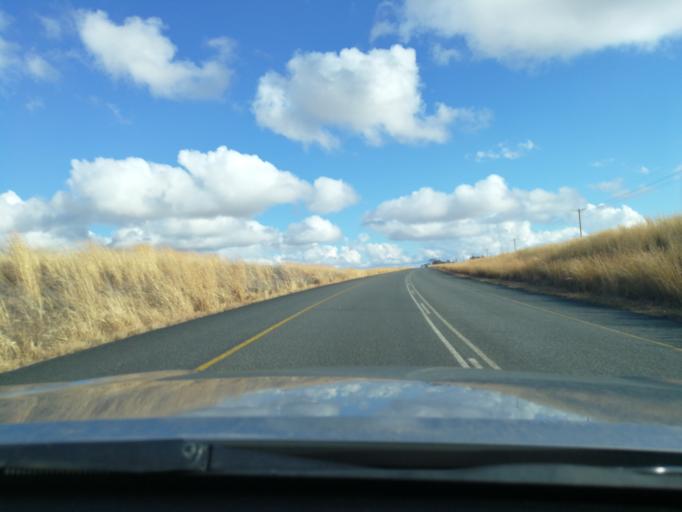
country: ZA
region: Orange Free State
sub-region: Thabo Mofutsanyana District Municipality
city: Reitz
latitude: -27.9621
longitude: 28.3803
